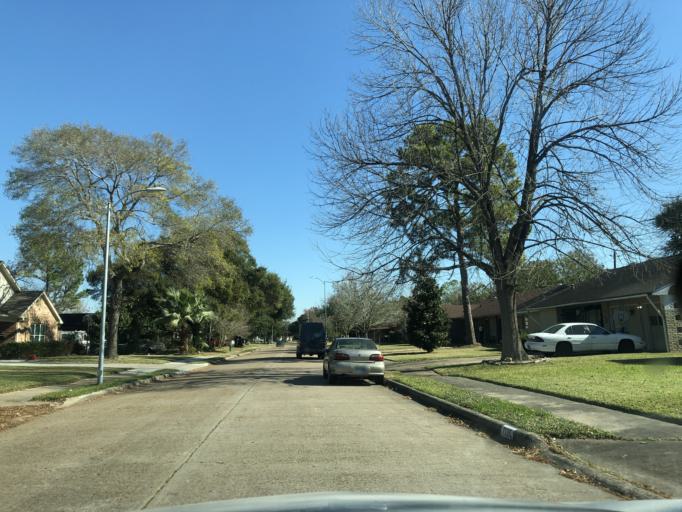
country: US
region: Texas
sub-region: Harris County
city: Bellaire
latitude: 29.6987
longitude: -95.5104
